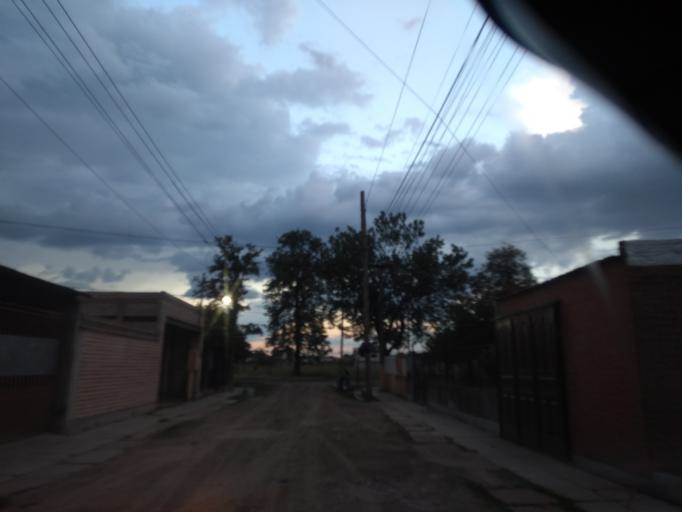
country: AR
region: Chaco
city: Fontana
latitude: -27.4160
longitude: -59.0383
